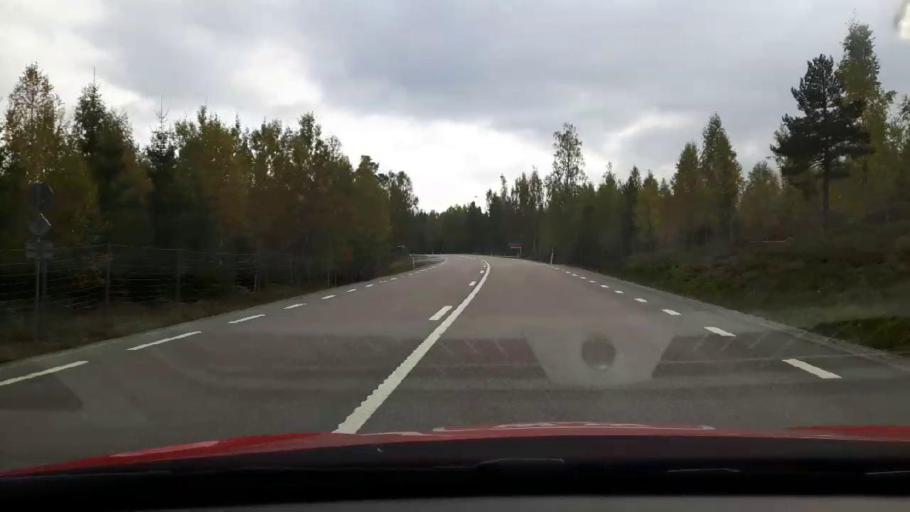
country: SE
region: Gaevleborg
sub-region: Bollnas Kommun
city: Kilafors
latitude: 61.2765
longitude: 16.5246
